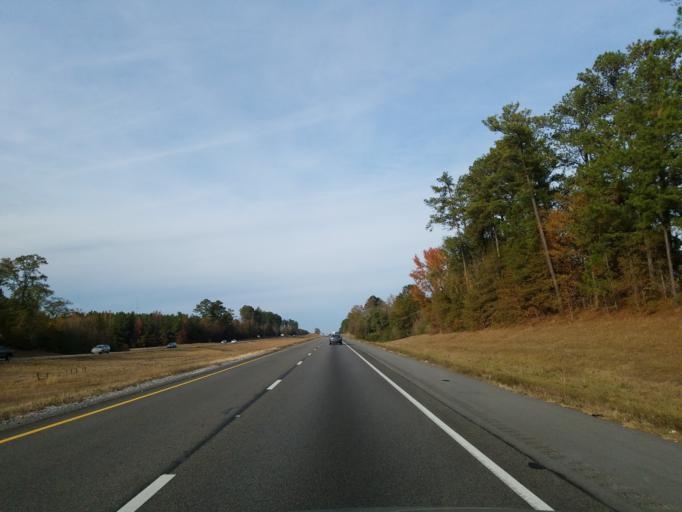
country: US
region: Mississippi
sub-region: Jones County
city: Sharon
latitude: 31.8142
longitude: -89.0523
